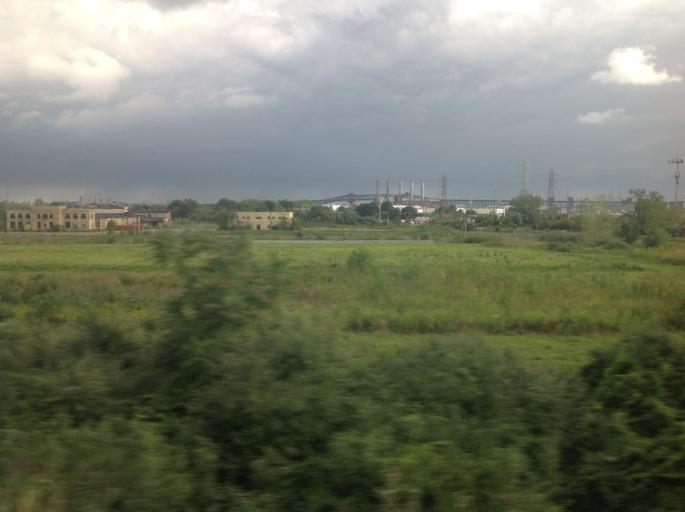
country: US
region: New Jersey
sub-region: Hudson County
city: Jersey City
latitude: 40.7510
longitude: -74.1025
